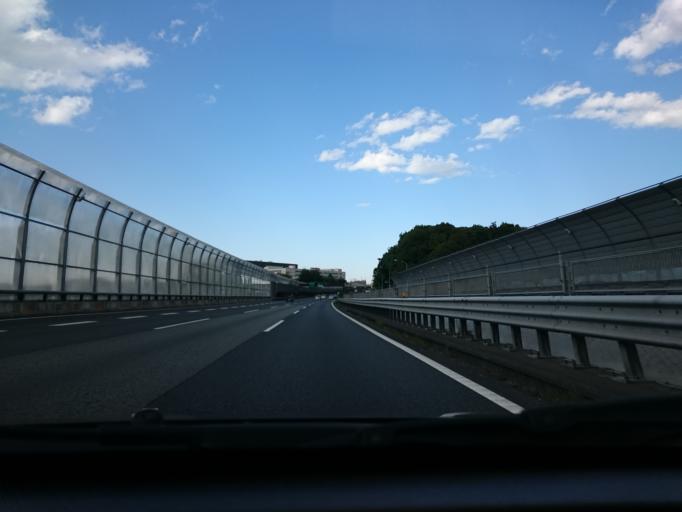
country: JP
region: Kanagawa
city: Atsugi
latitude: 35.4429
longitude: 139.4100
